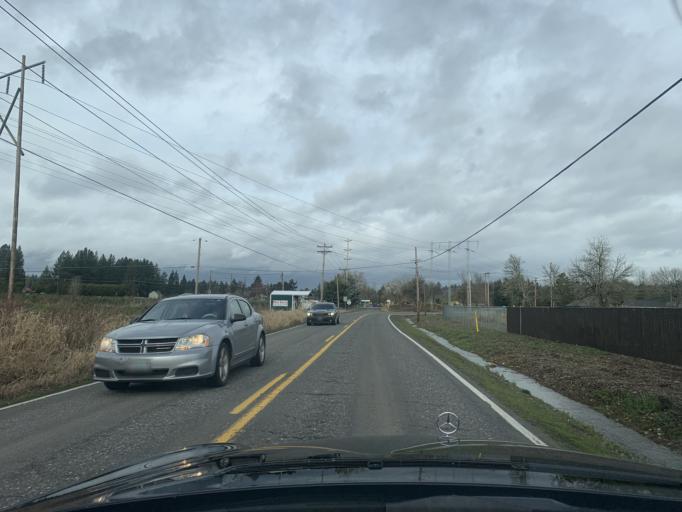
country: US
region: Oregon
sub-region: Clackamas County
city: Happy Valley
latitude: 45.4591
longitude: -122.4865
